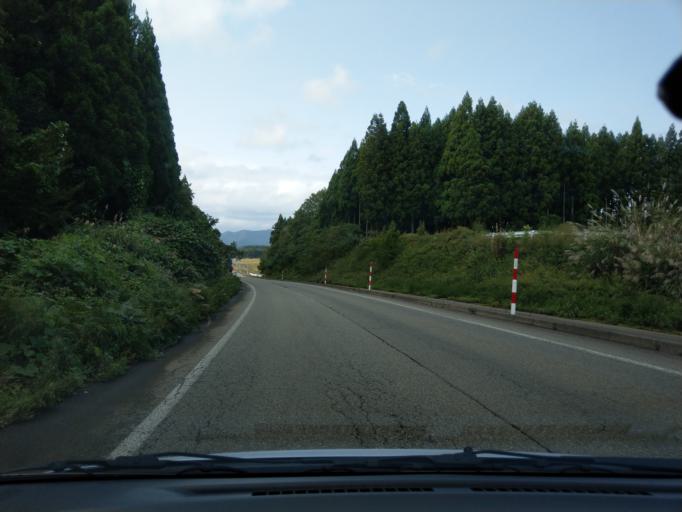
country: JP
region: Akita
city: Omagari
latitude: 39.5241
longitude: 140.2909
